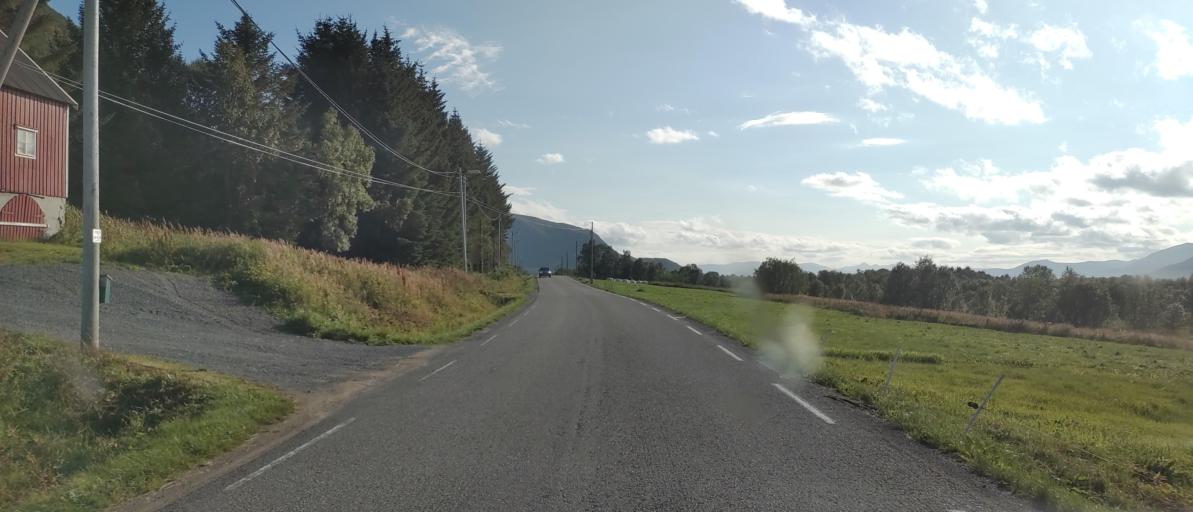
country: NO
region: Nordland
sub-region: Sortland
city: Sortland
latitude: 68.9228
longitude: 15.6193
